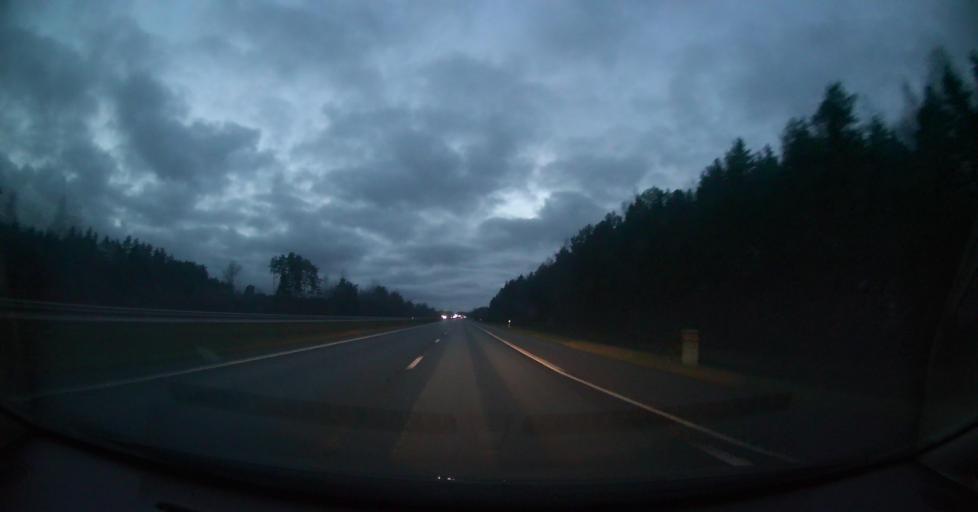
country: EE
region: Harju
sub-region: Kuusalu vald
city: Kuusalu
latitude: 59.4527
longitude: 25.4757
